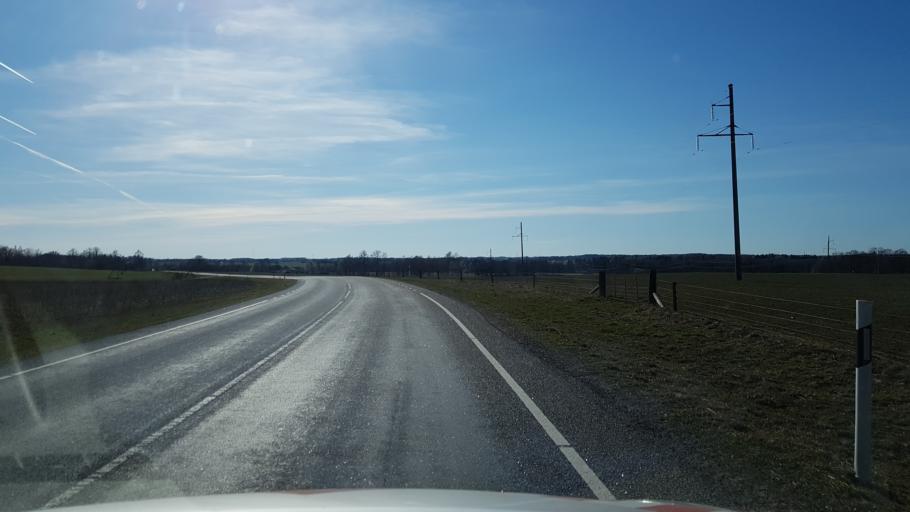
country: EE
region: Laeaene-Virumaa
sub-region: Vinni vald
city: Vinni
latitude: 59.3219
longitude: 26.4993
